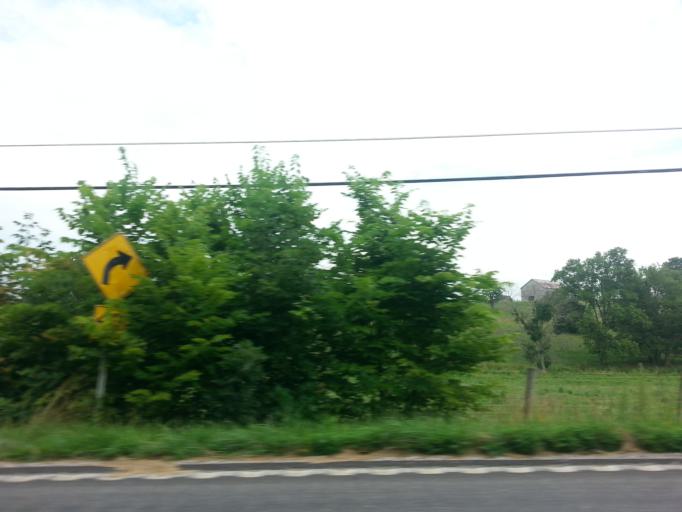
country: US
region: Kentucky
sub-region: Harrison County
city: Cynthiana
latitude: 38.4382
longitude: -84.2486
